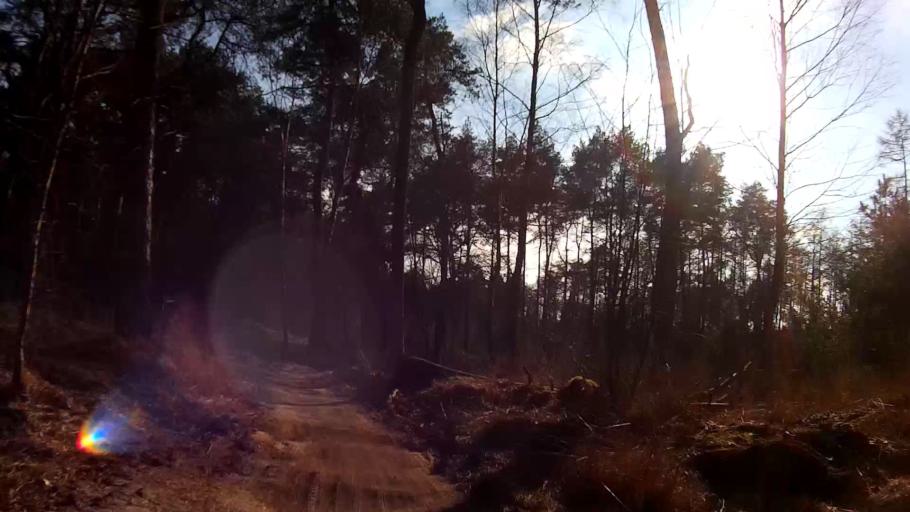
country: NL
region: Utrecht
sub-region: Gemeente Utrechtse Heuvelrug
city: Leersum
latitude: 52.0296
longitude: 5.4342
